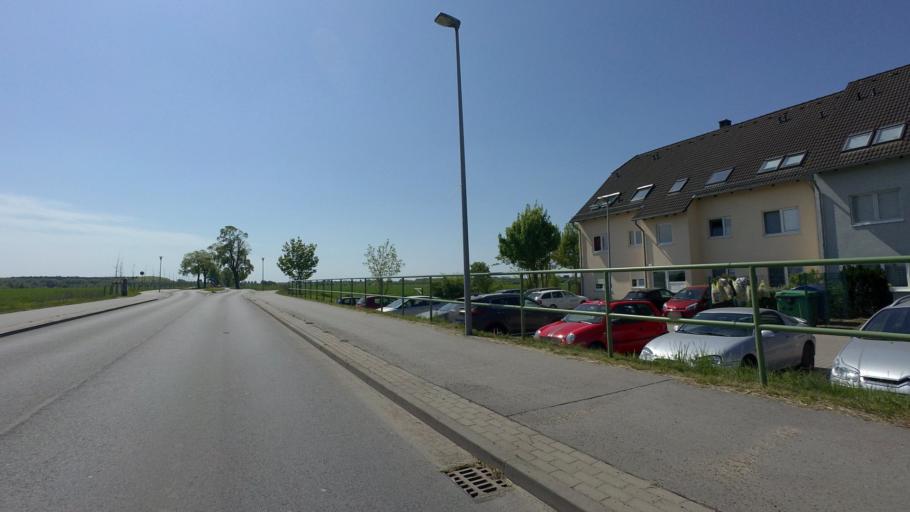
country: DE
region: Brandenburg
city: Schulzendorf
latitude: 52.3586
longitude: 13.5574
